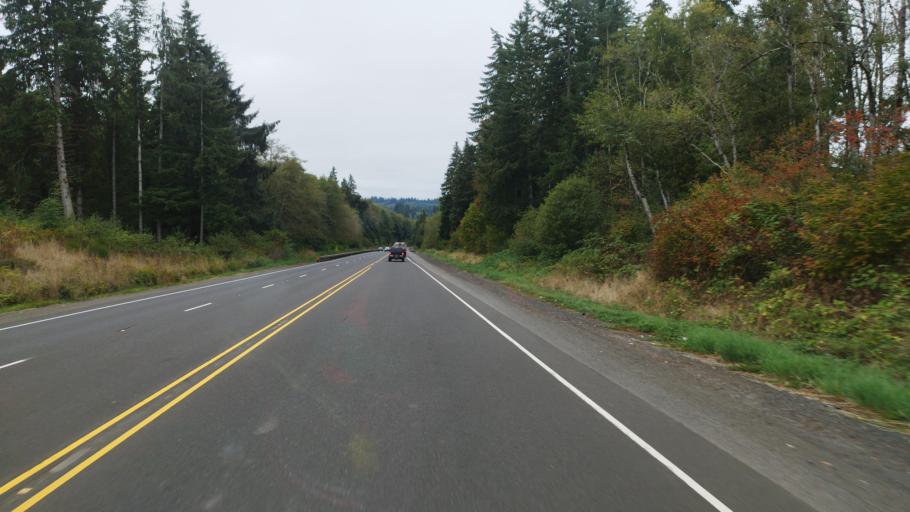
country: US
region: Washington
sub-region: Wahkiakum County
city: Cathlamet
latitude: 46.1710
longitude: -123.5589
